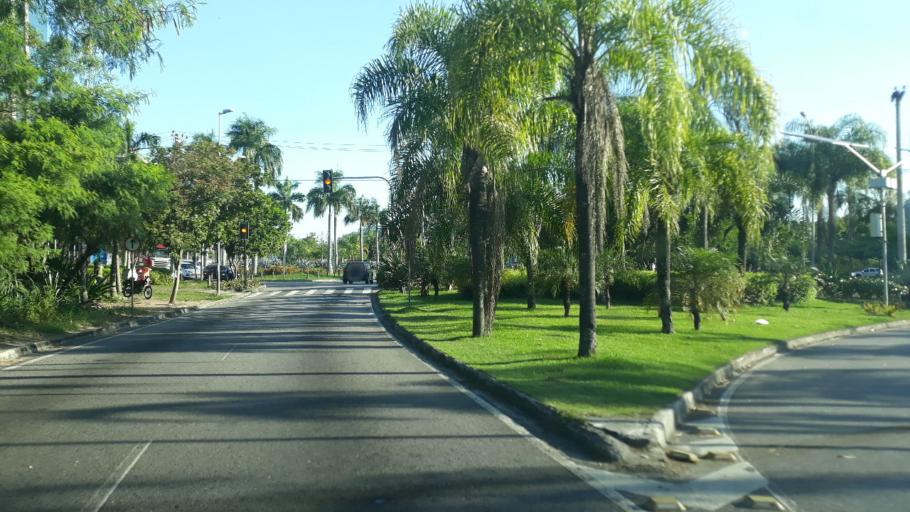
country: BR
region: Rio de Janeiro
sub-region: Rio De Janeiro
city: Rio de Janeiro
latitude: -22.9838
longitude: -43.3603
